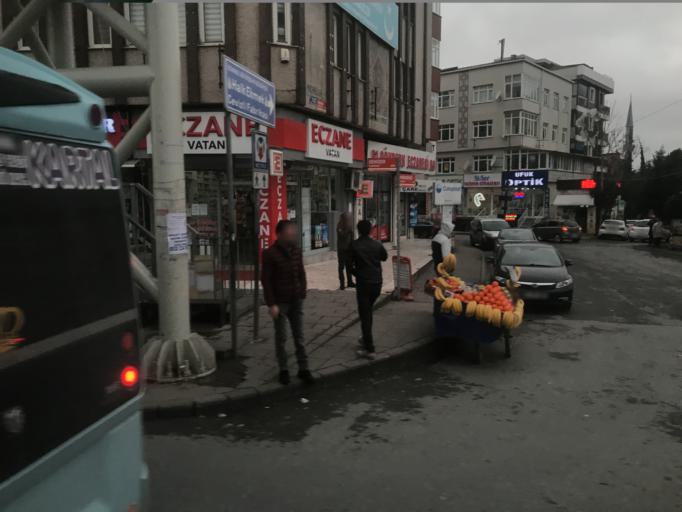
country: TR
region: Istanbul
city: Maltepe
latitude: 40.9159
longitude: 29.1700
